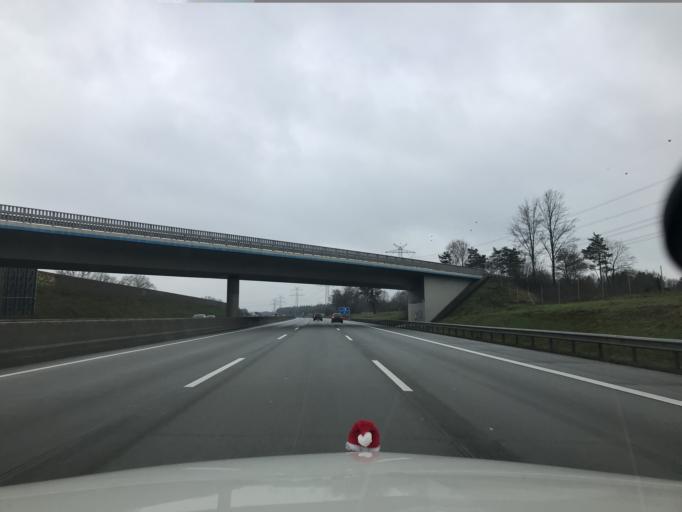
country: DE
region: Schleswig-Holstein
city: Kaltenkirchen
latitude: 53.8263
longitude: 9.9231
